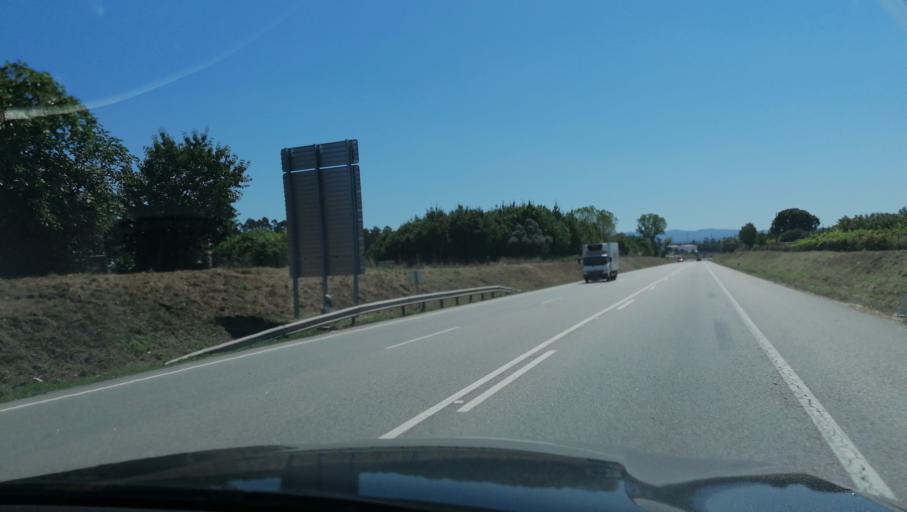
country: PT
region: Aveiro
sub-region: Oliveira do Bairro
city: Oliveira do Bairro
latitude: 40.5415
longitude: -8.4662
